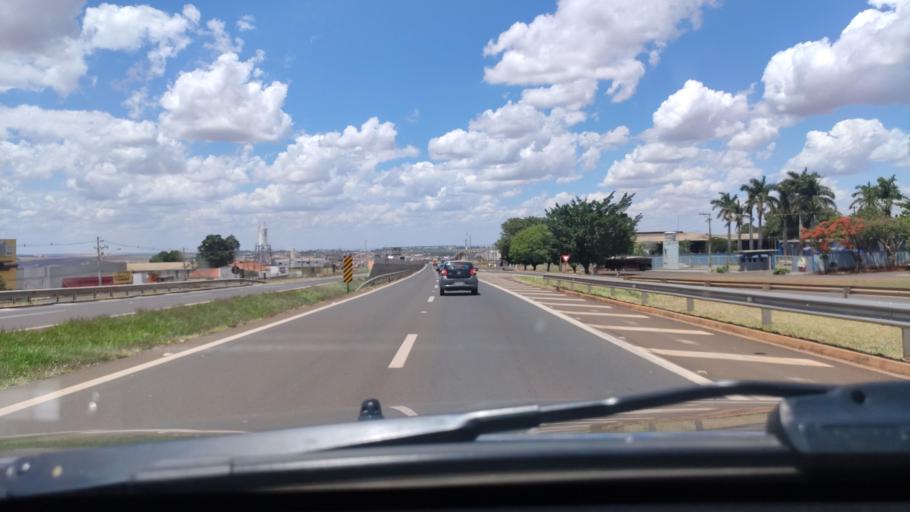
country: BR
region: Sao Paulo
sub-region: Jau
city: Jau
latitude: -22.2586
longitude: -48.5521
